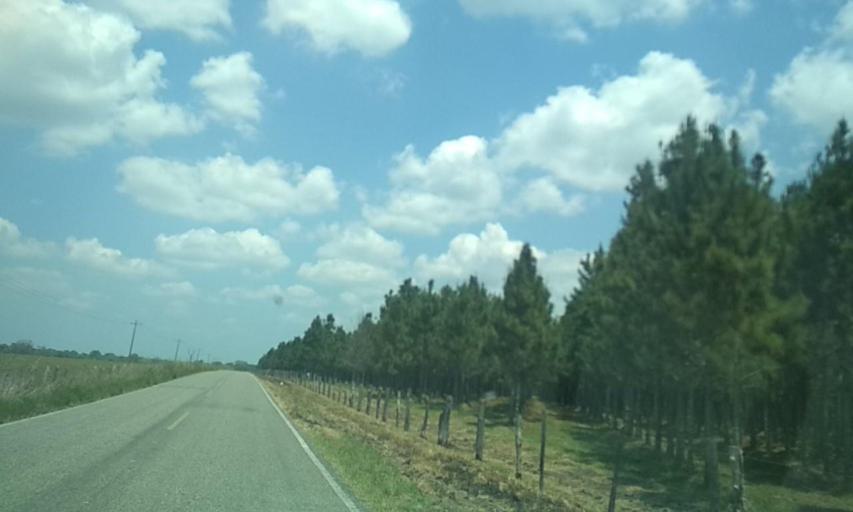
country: MX
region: Tabasco
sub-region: Huimanguillo
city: Huapacal 1ra. Seccion
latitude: 17.7561
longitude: -93.7649
